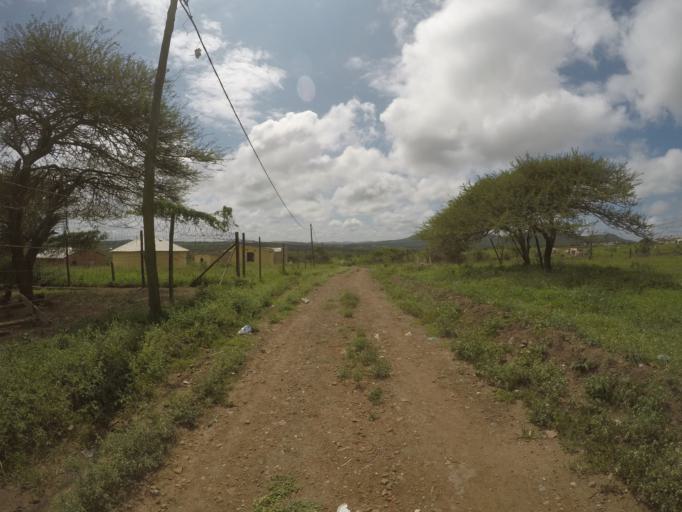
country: ZA
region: KwaZulu-Natal
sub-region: uThungulu District Municipality
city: Empangeni
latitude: -28.5731
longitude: 31.8402
